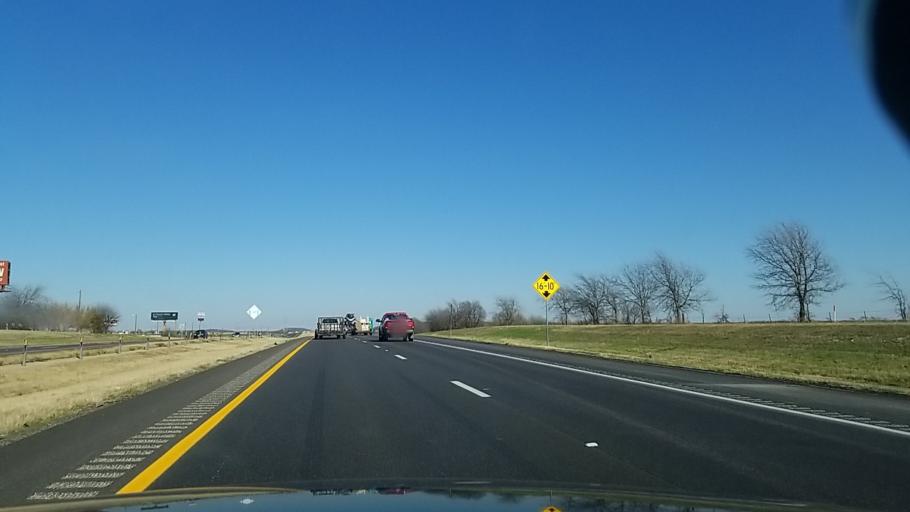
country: US
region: Texas
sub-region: Denton County
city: Northlake
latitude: 33.0948
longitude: -97.2273
